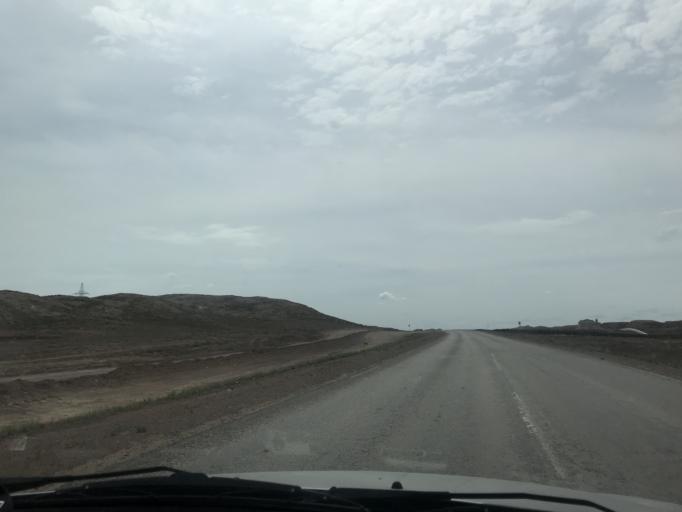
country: KZ
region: Zhambyl
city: Mynaral
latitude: 45.3713
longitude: 73.6579
